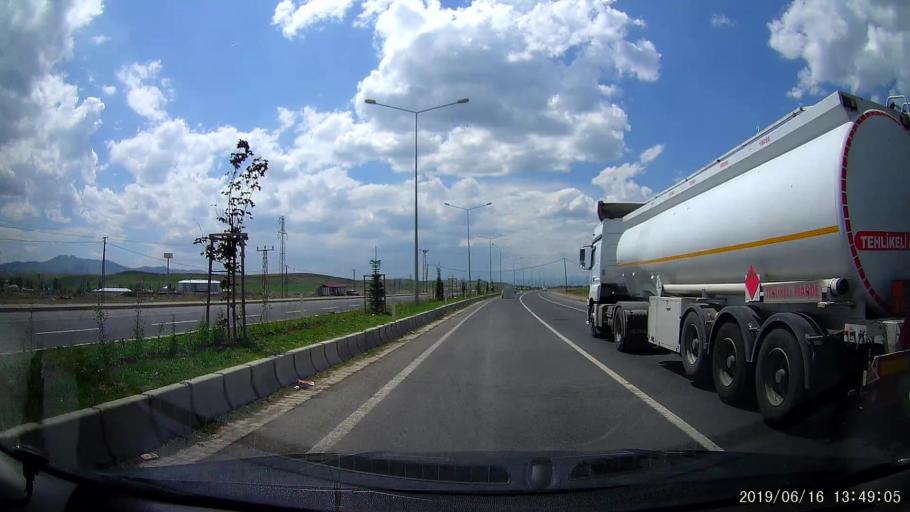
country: TR
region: Agri
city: Agri
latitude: 39.7152
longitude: 42.9956
